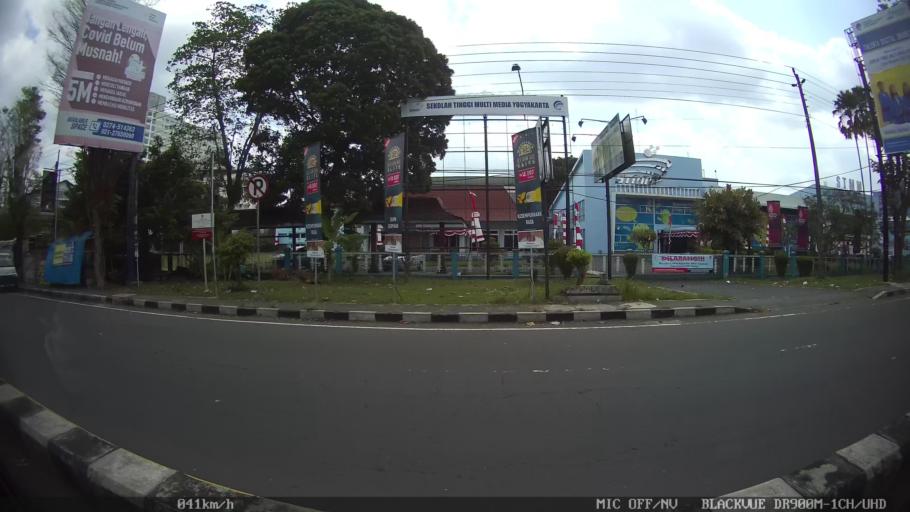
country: ID
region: Daerah Istimewa Yogyakarta
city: Melati
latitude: -7.7512
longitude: 110.3623
